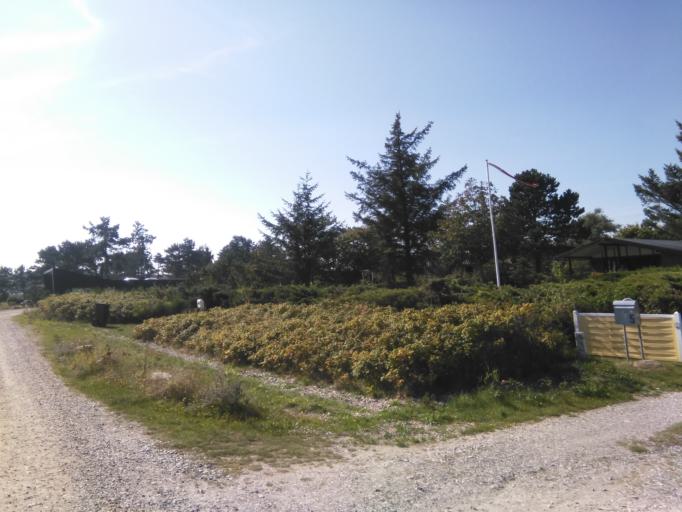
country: DK
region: Central Jutland
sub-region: Syddjurs Kommune
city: Ebeltoft
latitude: 56.2237
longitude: 10.7404
